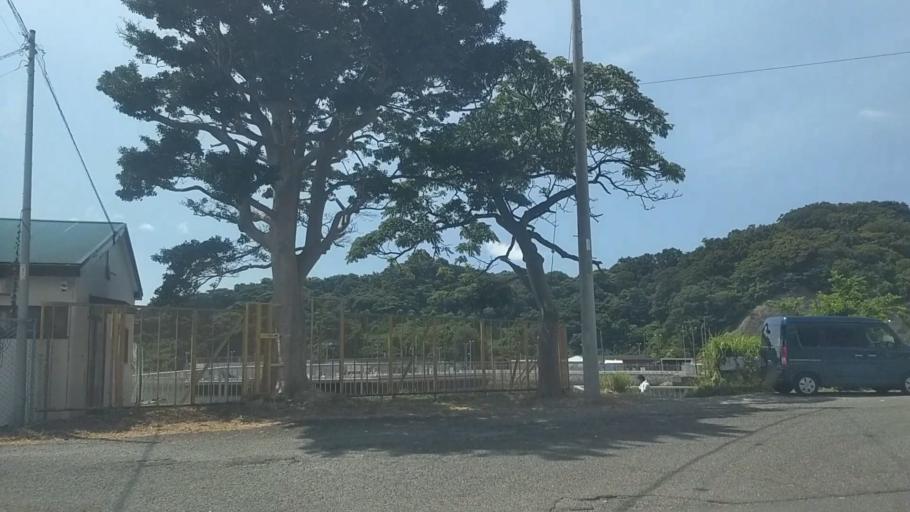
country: JP
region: Kanagawa
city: Yokosuka
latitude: 35.3080
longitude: 139.6422
